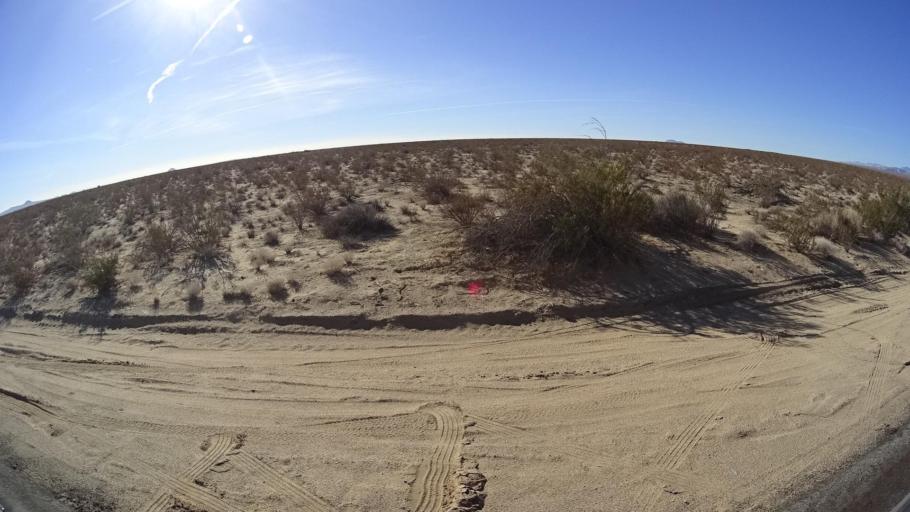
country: US
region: California
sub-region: Kern County
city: California City
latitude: 35.1986
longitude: -118.0401
